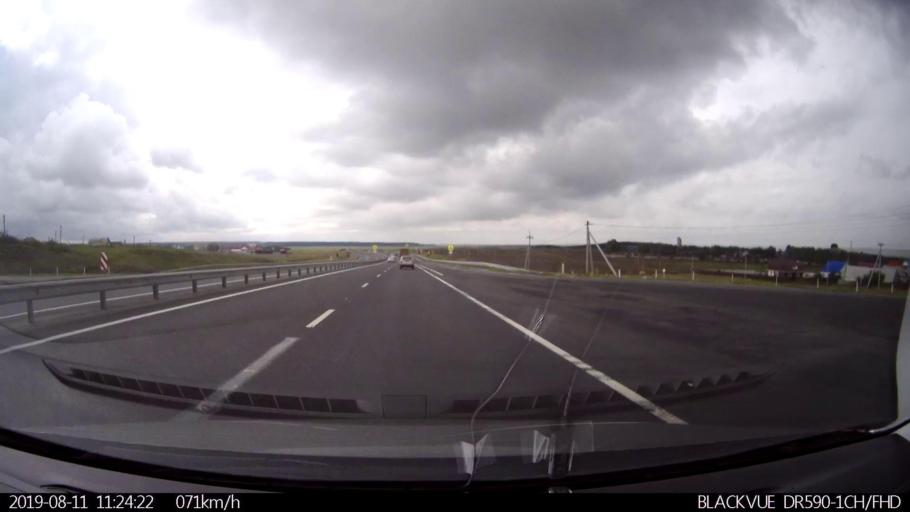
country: RU
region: Ulyanovsk
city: Krasnyy Gulyay
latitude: 54.1277
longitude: 48.2431
